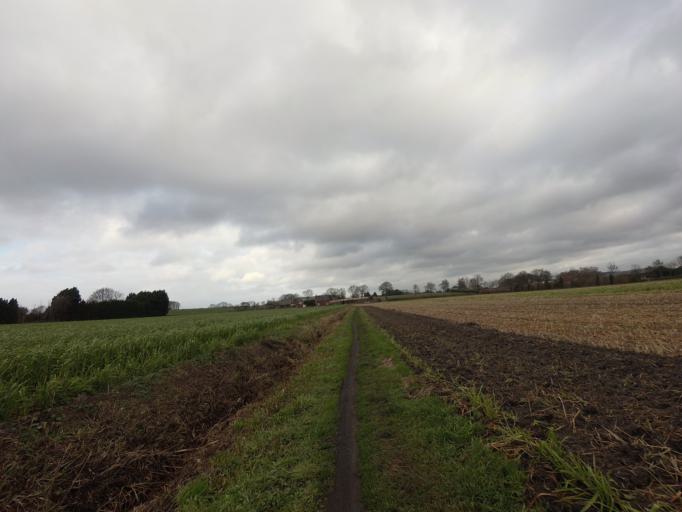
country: NL
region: North Brabant
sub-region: Gemeente Woensdrecht
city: Woensdrecht
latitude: 51.3810
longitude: 4.3338
